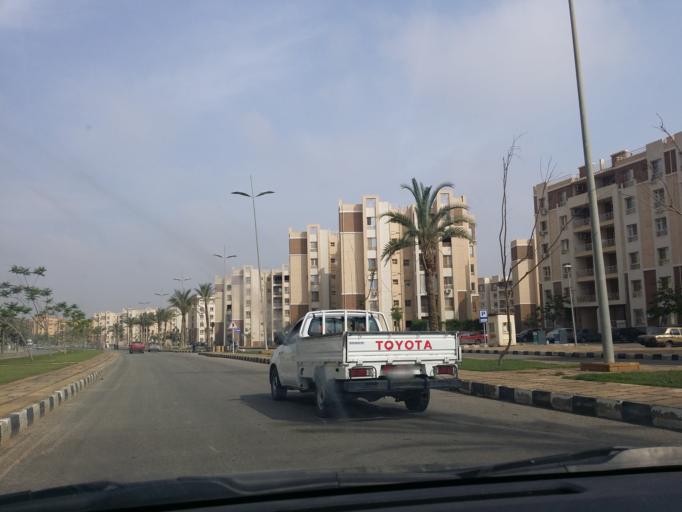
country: EG
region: Muhafazat al Qalyubiyah
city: Al Khankah
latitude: 30.0834
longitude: 31.6482
